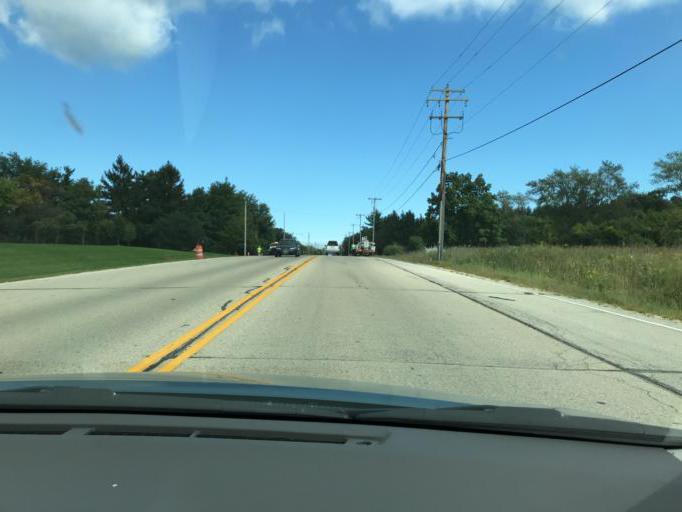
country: US
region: Wisconsin
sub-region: Kenosha County
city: Pleasant Prairie
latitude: 42.5229
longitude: -87.8848
